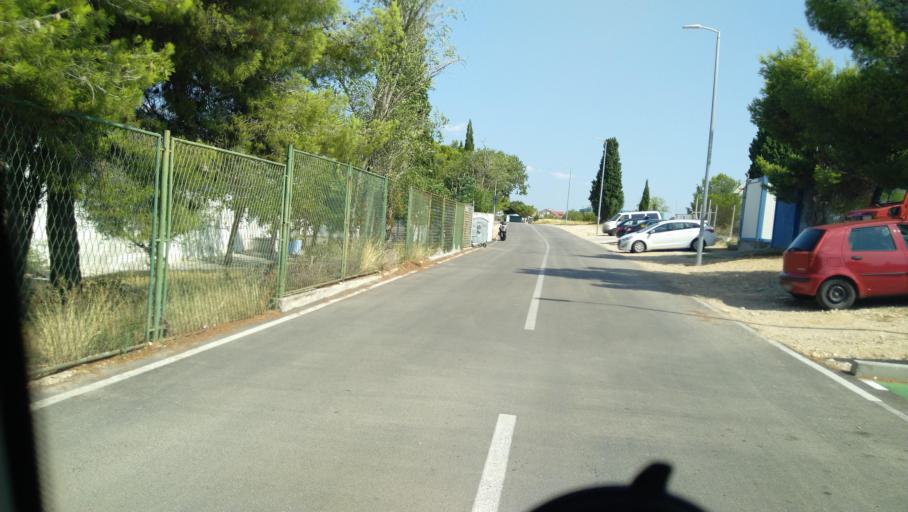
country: HR
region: Sibensko-Kniniska
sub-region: Grad Sibenik
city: Sibenik
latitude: 43.7165
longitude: 15.9082
